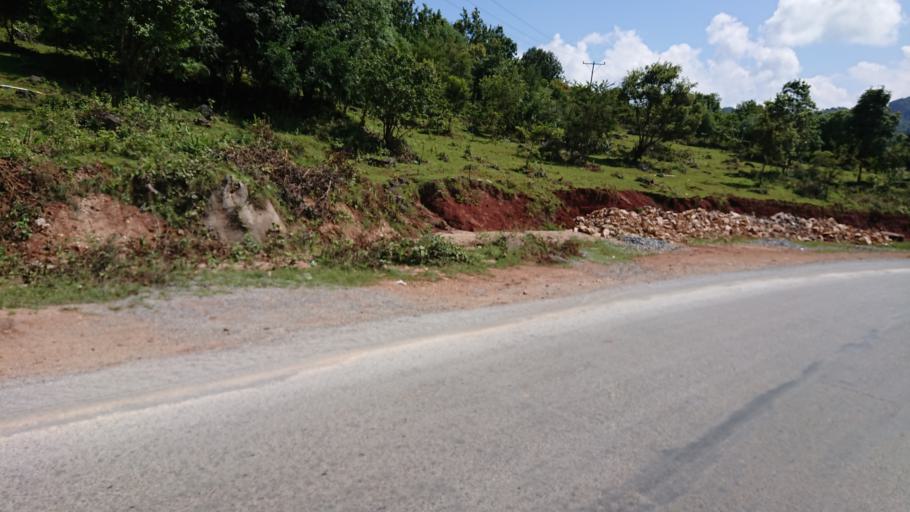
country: MM
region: Shan
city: Taunggyi
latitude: 20.8153
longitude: 97.3283
